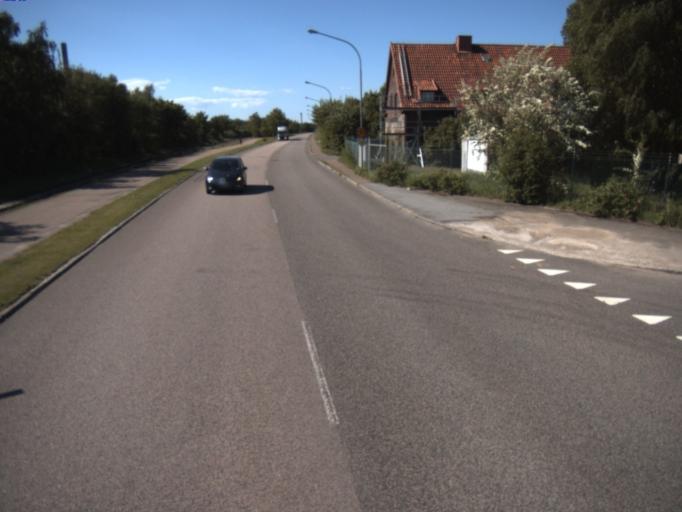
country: SE
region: Skane
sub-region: Helsingborg
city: Helsingborg
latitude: 56.0093
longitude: 12.7222
